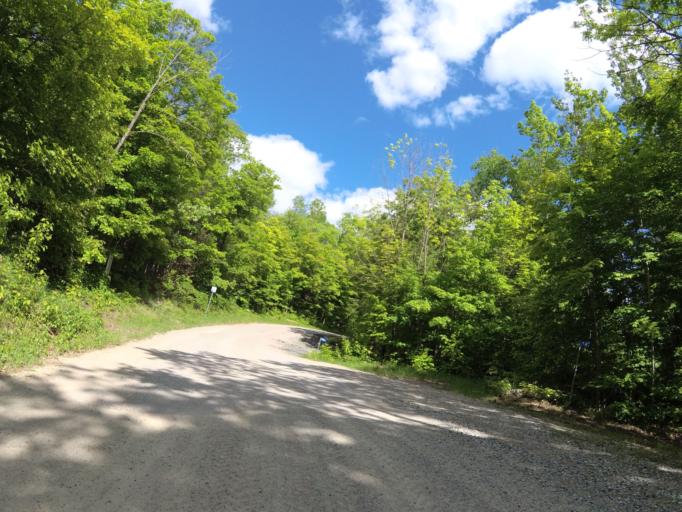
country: CA
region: Ontario
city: Renfrew
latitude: 45.0408
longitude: -76.8194
